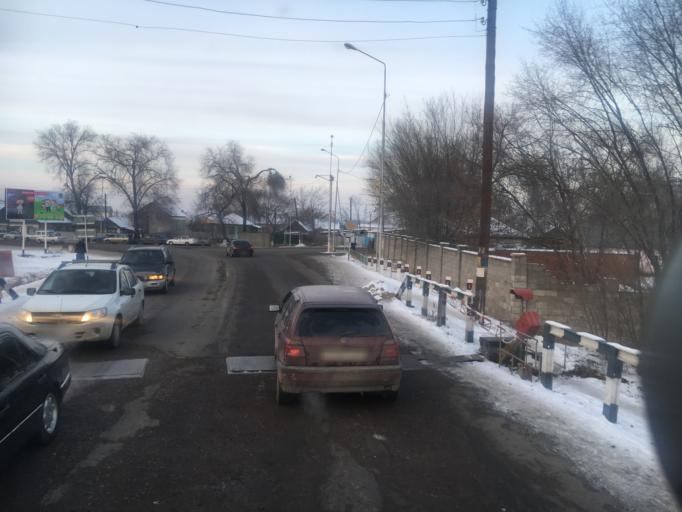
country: KZ
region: Almaty Oblysy
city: Burunday
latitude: 43.3767
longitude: 76.6419
